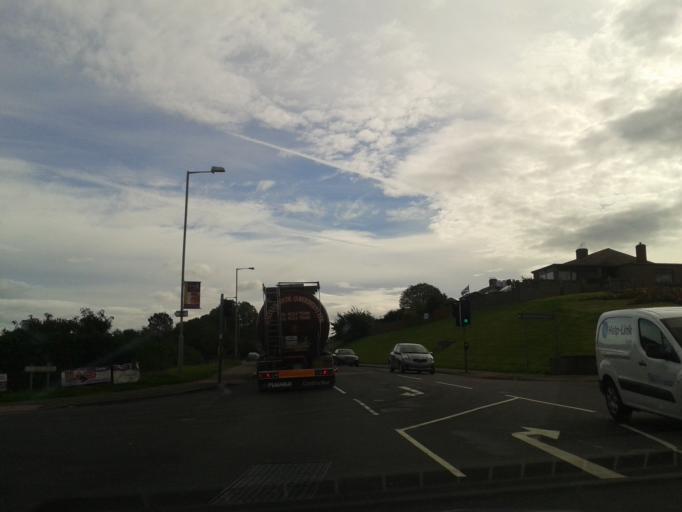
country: GB
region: Scotland
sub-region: Highland
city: Nairn
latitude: 57.5851
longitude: -3.8629
